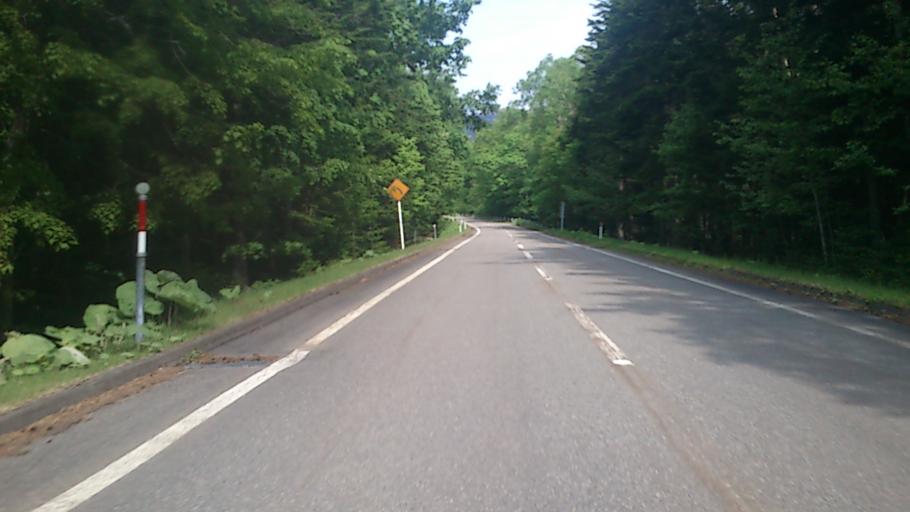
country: JP
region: Hokkaido
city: Kitami
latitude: 43.4019
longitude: 143.9755
